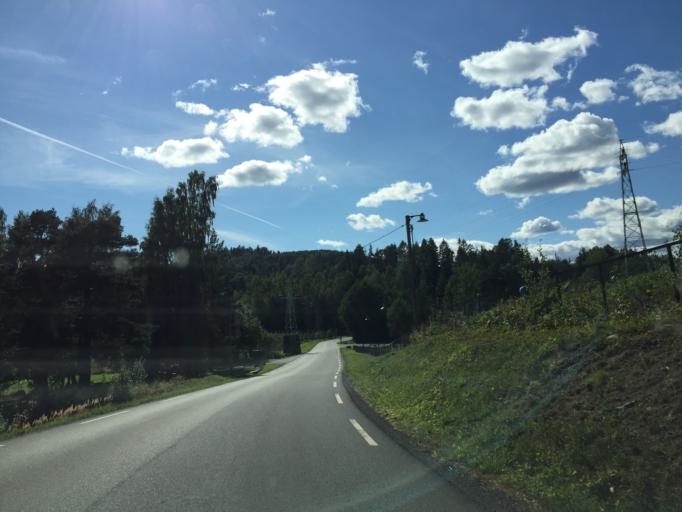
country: NO
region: Buskerud
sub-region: Ovre Eiker
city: Hokksund
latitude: 59.6972
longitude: 9.8438
